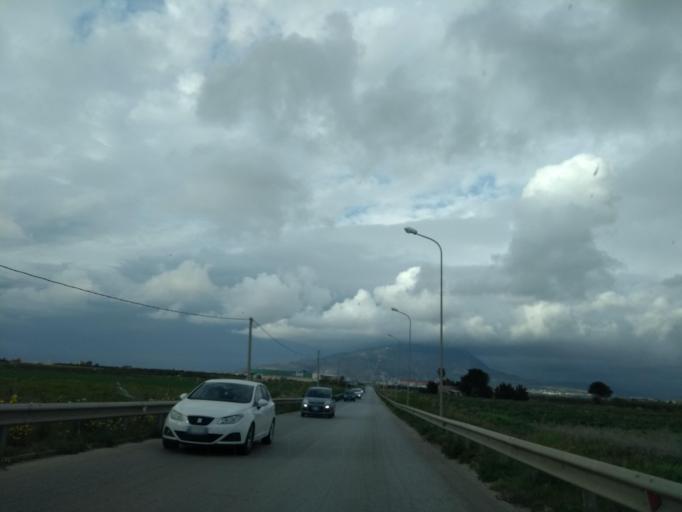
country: IT
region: Sicily
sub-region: Trapani
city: Marausa
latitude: 37.9706
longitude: 12.5233
